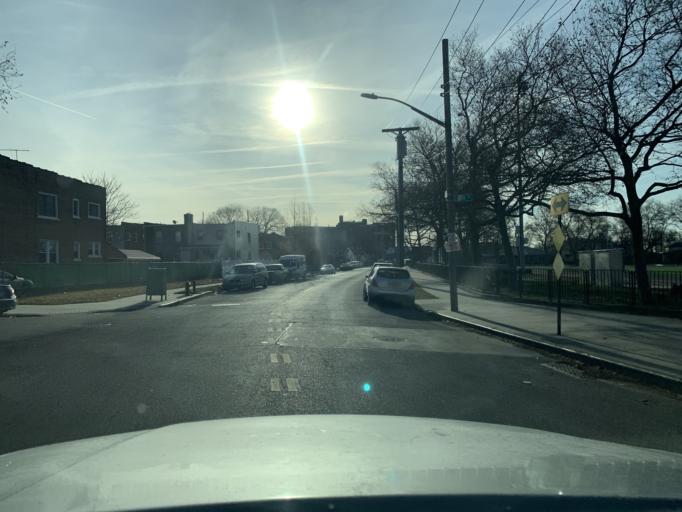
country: US
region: New York
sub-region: Queens County
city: Jamaica
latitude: 40.7034
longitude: -73.7841
